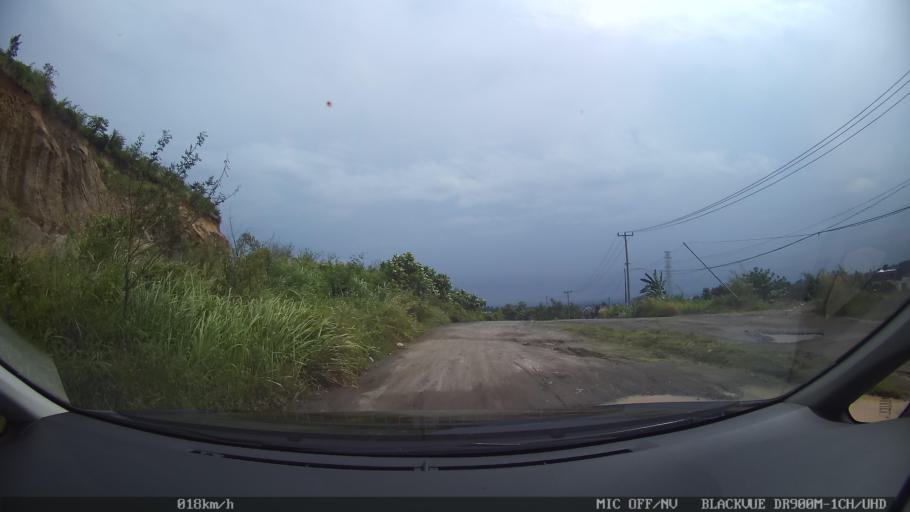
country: ID
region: Lampung
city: Bandarlampung
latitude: -5.4126
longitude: 105.1970
